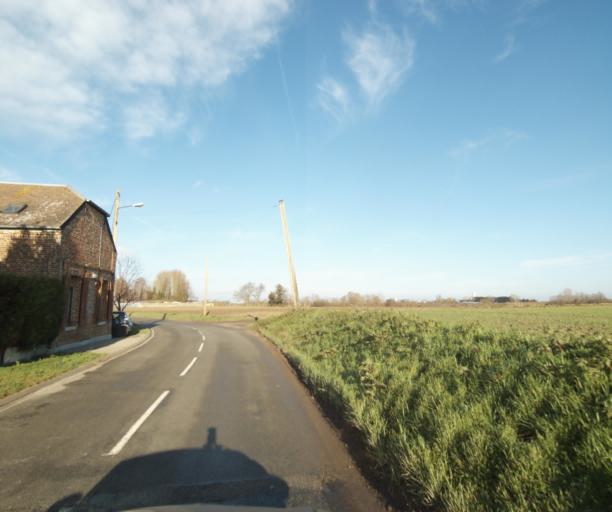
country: FR
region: Nord-Pas-de-Calais
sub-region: Departement du Nord
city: Saultain
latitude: 50.3277
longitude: 3.5754
